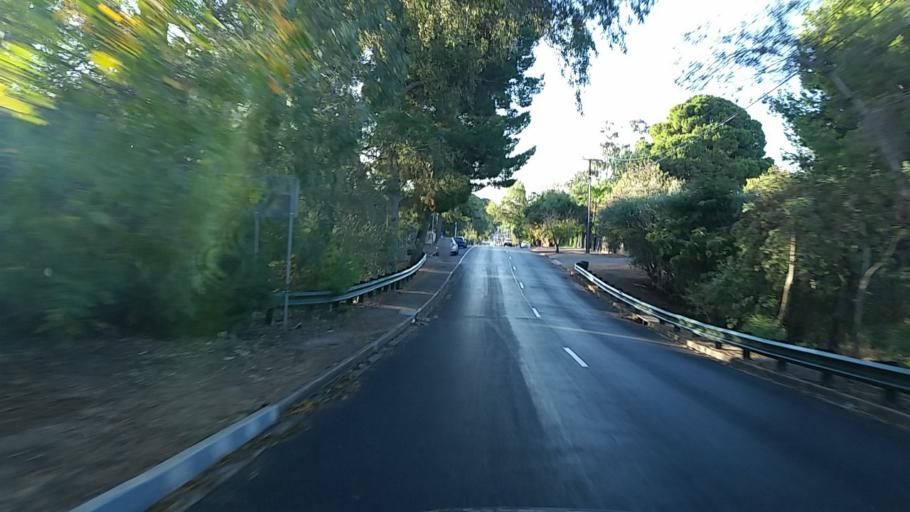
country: AU
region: South Australia
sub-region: Mitcham
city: Mitcham
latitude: -34.9812
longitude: 138.6277
